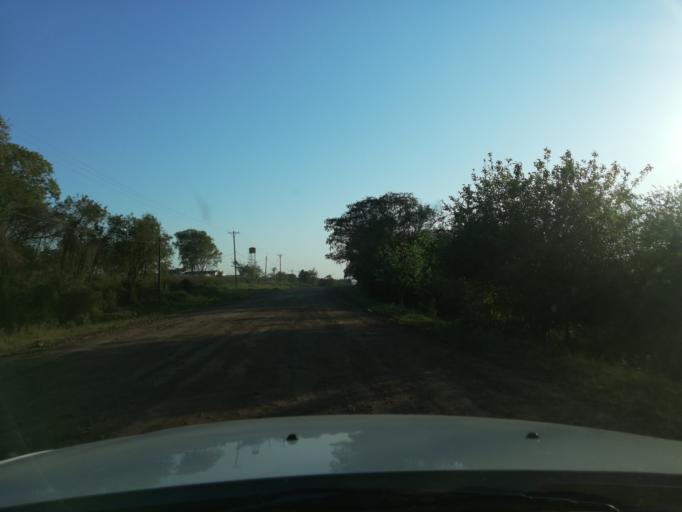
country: AR
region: Misiones
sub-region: Departamento de Apostoles
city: San Jose
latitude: -27.6318
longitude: -55.7294
